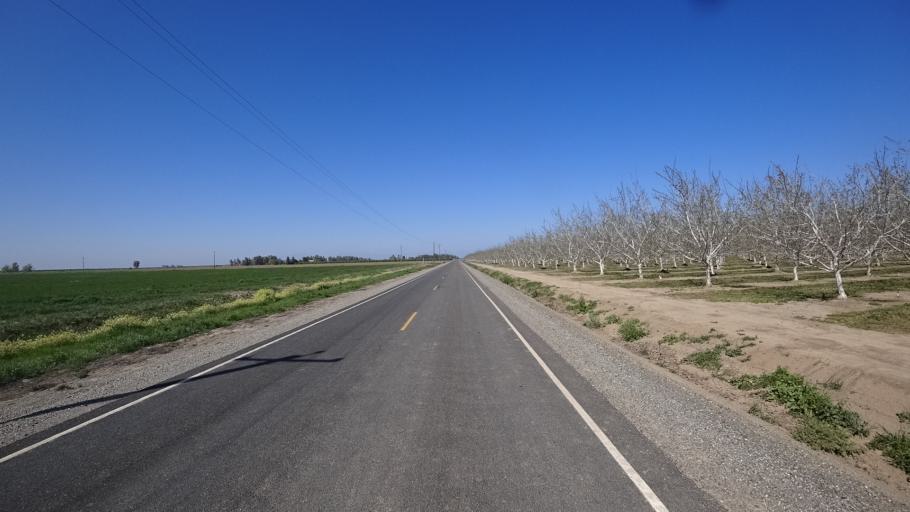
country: US
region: California
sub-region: Glenn County
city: Hamilton City
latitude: 39.6597
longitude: -122.0377
